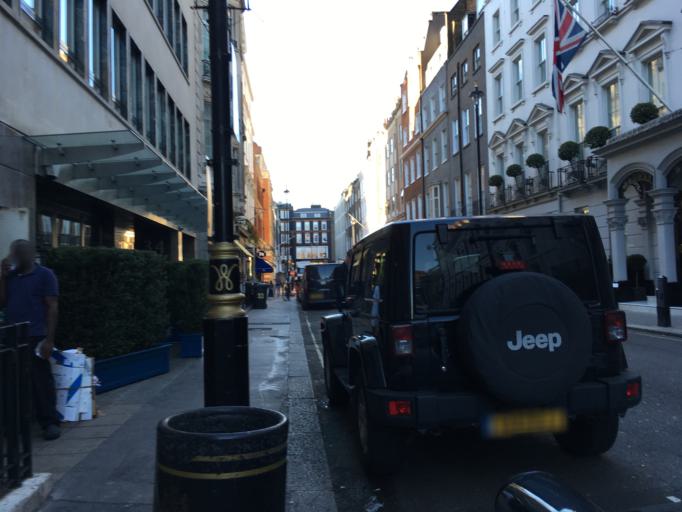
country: GB
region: England
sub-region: Greater London
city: London
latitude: 51.5088
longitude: -0.1425
